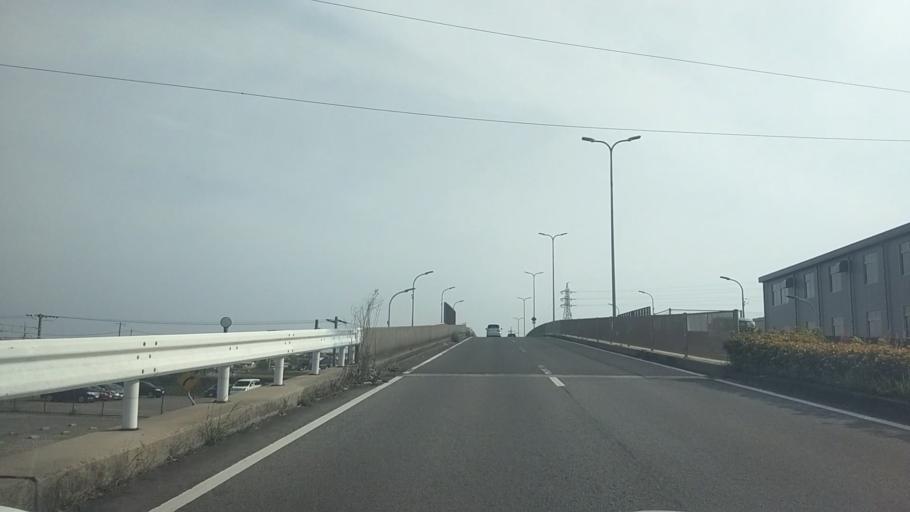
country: JP
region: Aichi
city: Anjo
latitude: 34.9651
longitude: 137.0719
